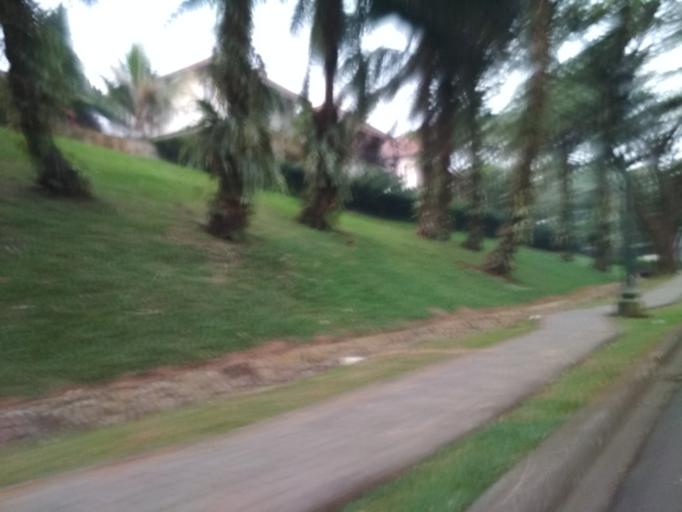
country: ID
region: West Java
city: Caringin
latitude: -6.6622
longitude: 106.8388
